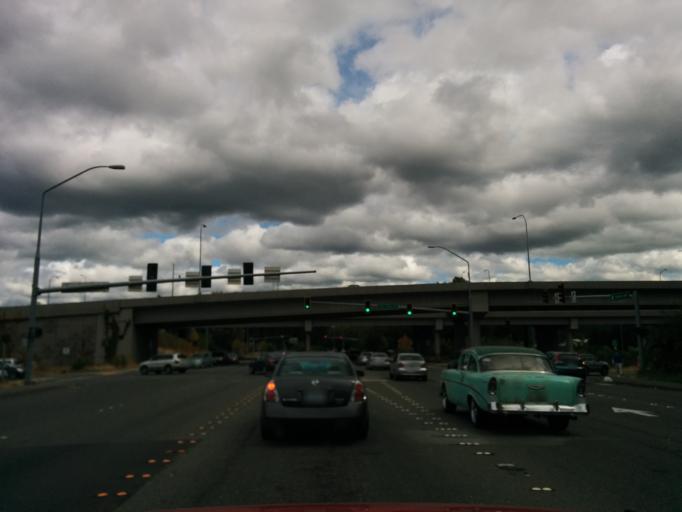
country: US
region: Washington
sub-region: King County
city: Redmond
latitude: 47.6702
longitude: -122.1091
